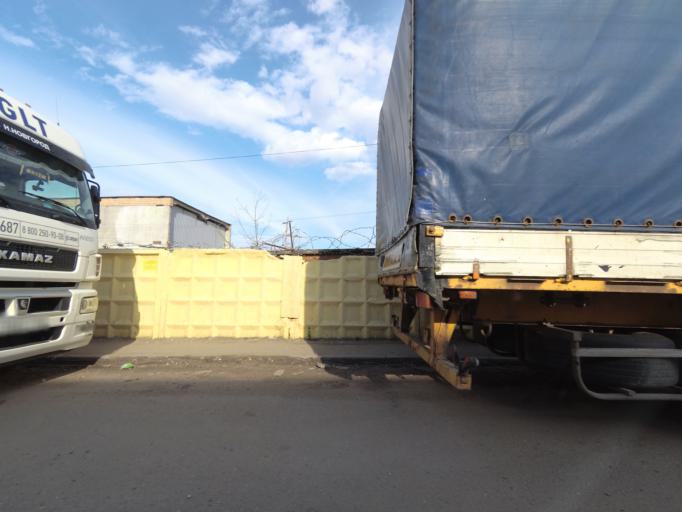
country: RU
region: Moskovskaya
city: Lobnya
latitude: 56.0168
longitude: 37.4363
